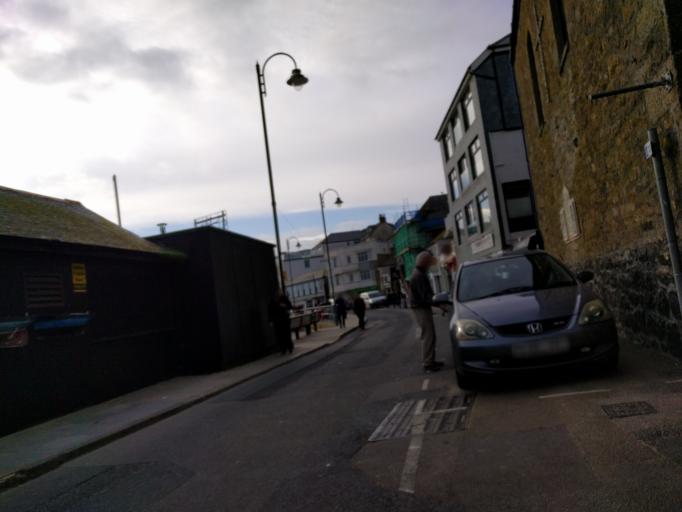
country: GB
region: England
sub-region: Cornwall
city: St Ives
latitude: 50.2148
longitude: -5.4797
